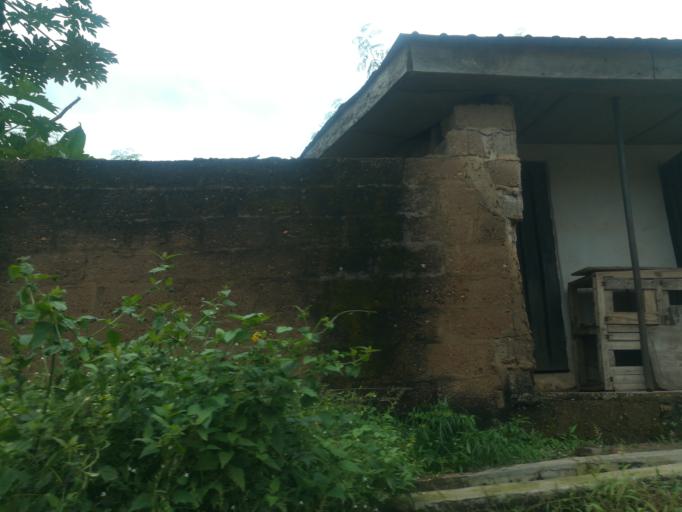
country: NG
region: Oyo
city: Ibadan
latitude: 7.3186
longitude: 3.8843
